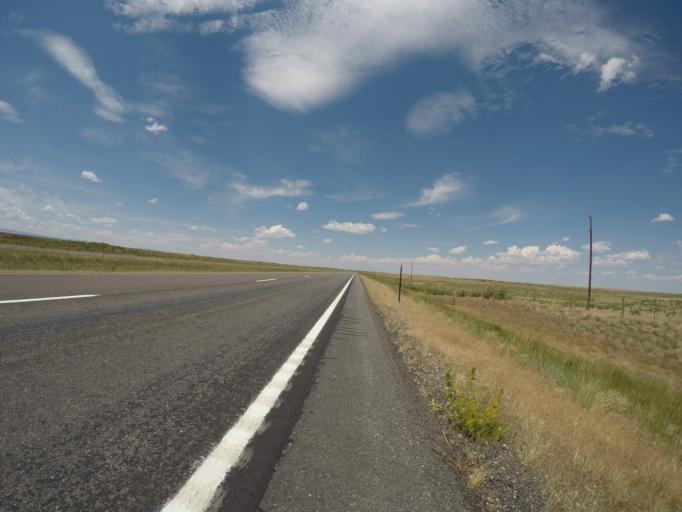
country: US
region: Wyoming
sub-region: Albany County
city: Laramie
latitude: 41.6191
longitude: -105.7472
